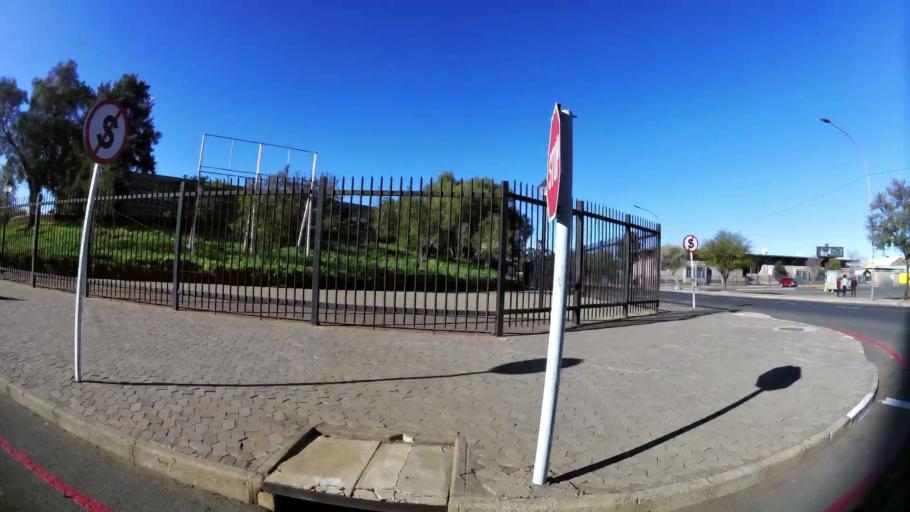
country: ZA
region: Northern Cape
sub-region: Frances Baard District Municipality
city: Kimberley
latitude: -28.7446
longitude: 24.7656
